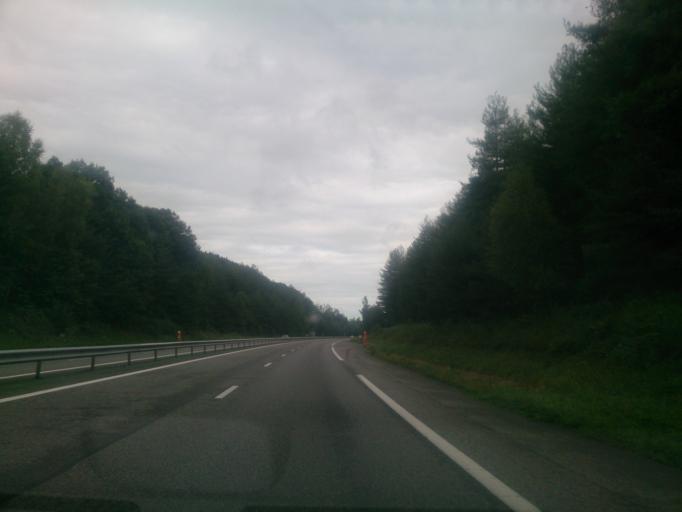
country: FR
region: Midi-Pyrenees
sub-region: Departement de la Haute-Garonne
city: Montrejeau
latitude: 43.0921
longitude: 0.5087
